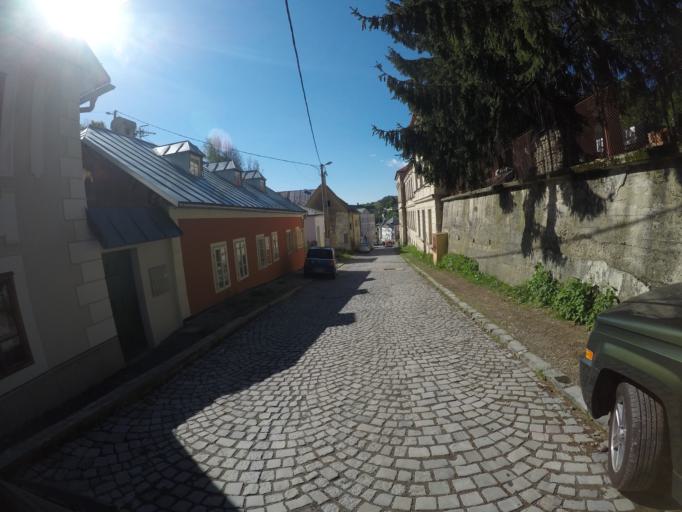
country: SK
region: Banskobystricky
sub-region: Okres Banska Bystrica
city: Banska Stiavnica
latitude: 48.4618
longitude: 18.8915
